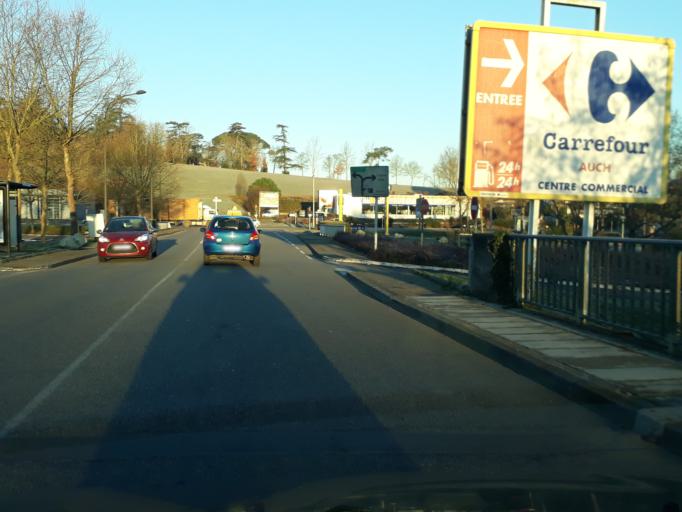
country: FR
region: Midi-Pyrenees
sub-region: Departement du Gers
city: Auch
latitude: 43.6307
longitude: 0.5827
